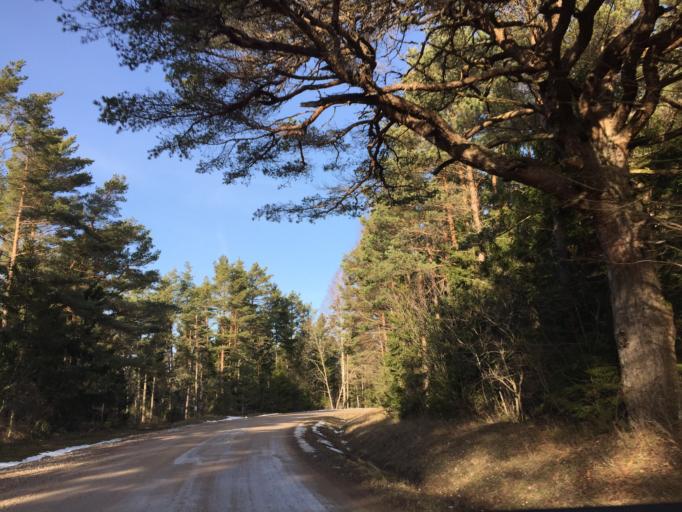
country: EE
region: Saare
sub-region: Kuressaare linn
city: Kuressaare
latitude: 58.3716
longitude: 22.0156
